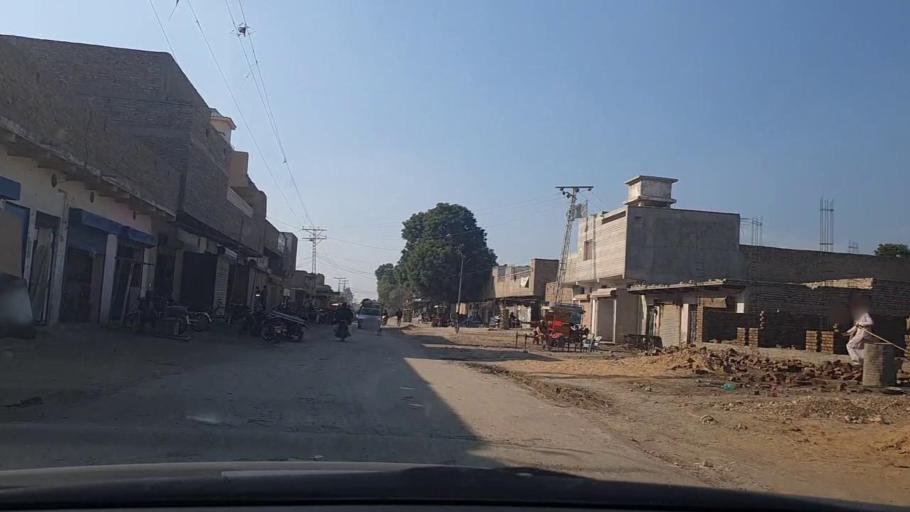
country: PK
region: Sindh
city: Daulatpur
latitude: 26.3028
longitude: 68.0970
